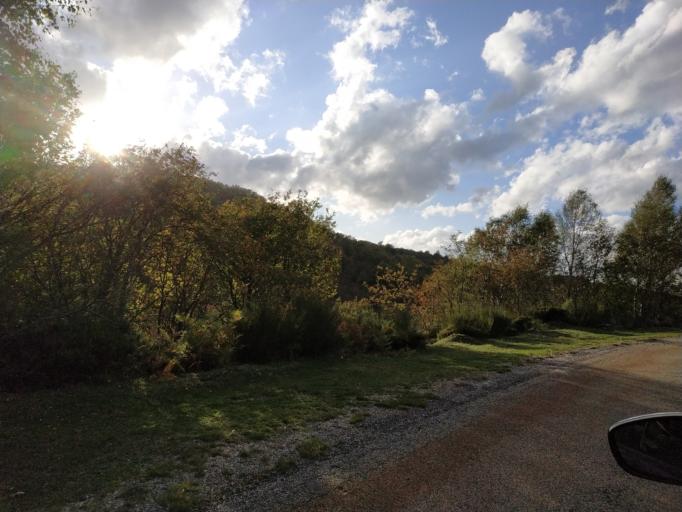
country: ES
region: Castille and Leon
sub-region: Provincia de Leon
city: Candin
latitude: 42.8746
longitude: -6.8308
